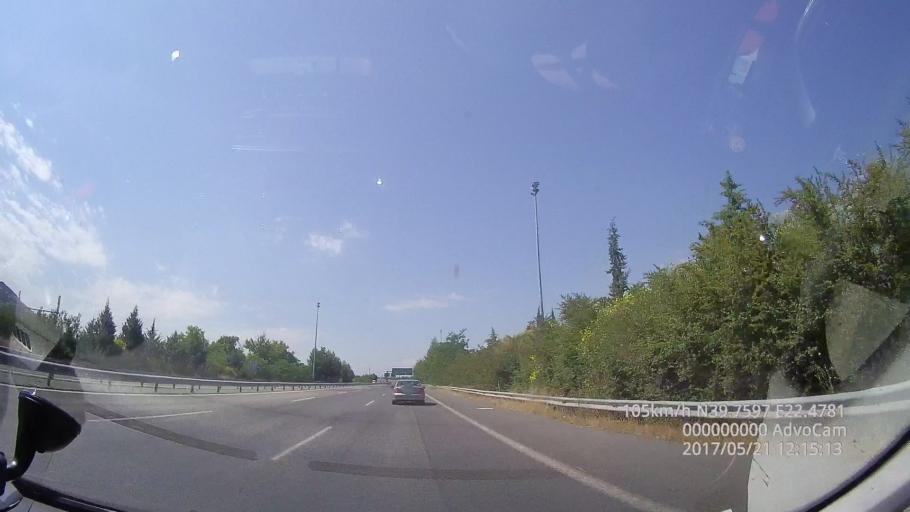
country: GR
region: Thessaly
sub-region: Nomos Larisis
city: Makrychori
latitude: 39.7592
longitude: 22.4779
